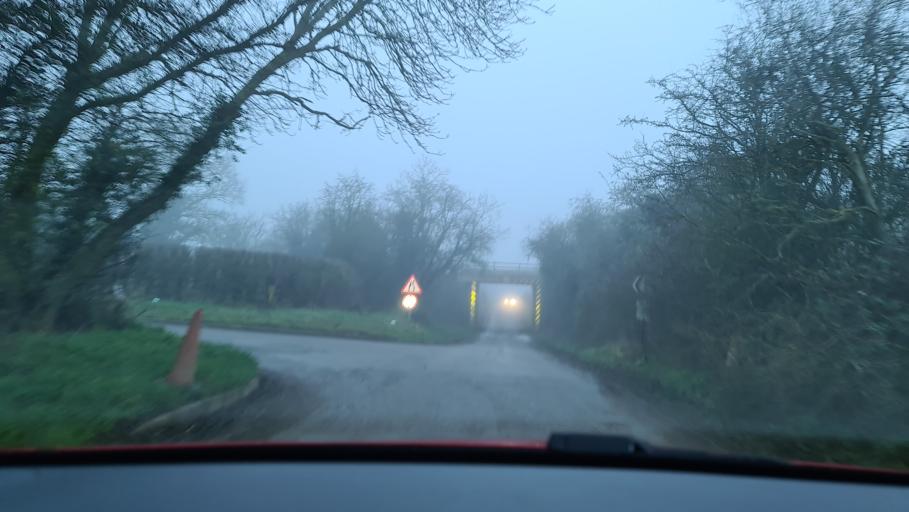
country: GB
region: England
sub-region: Buckinghamshire
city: Steeple Claydon
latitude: 51.8832
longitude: -0.9670
